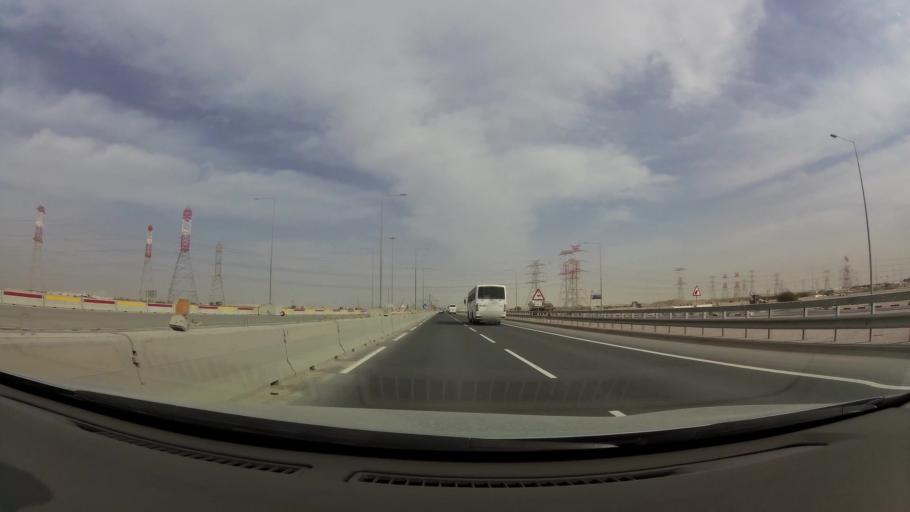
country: QA
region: Baladiyat ar Rayyan
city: Ash Shahaniyah
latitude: 25.3440
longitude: 51.3111
